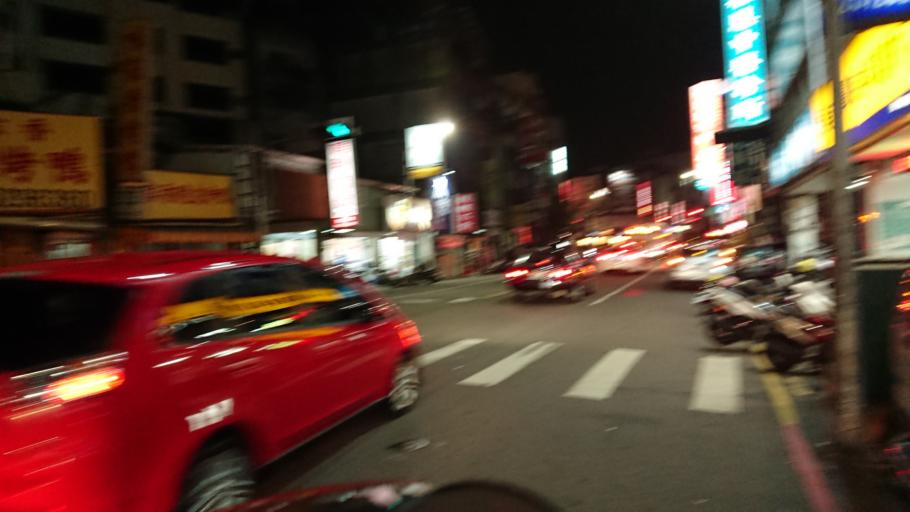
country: TW
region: Taiwan
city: Fengyuan
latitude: 24.2493
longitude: 120.7150
